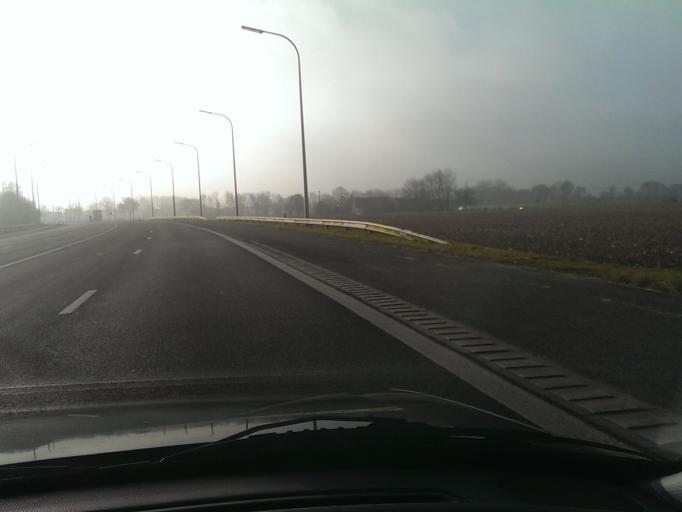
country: BE
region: Flanders
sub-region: Provincie West-Vlaanderen
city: Roeselare
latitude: 50.9305
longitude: 3.1032
